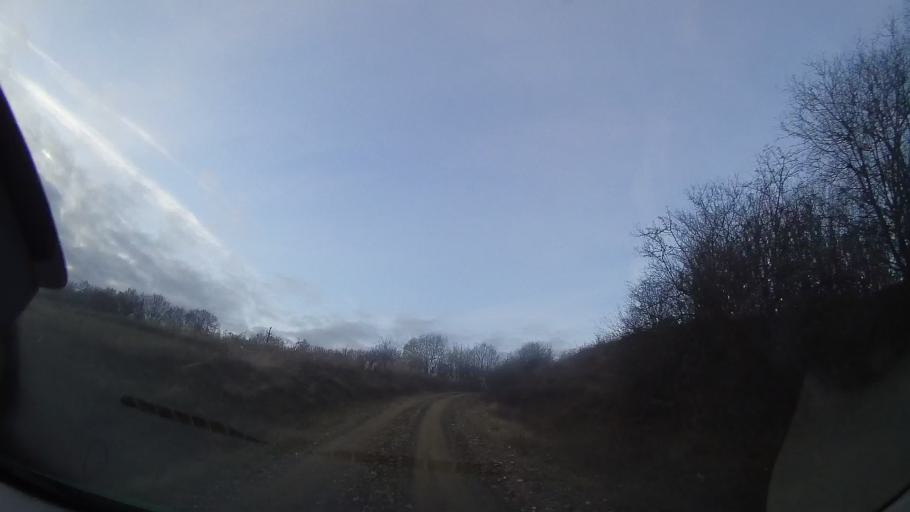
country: RO
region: Cluj
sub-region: Comuna Palatca
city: Palatca
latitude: 46.8593
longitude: 24.0267
